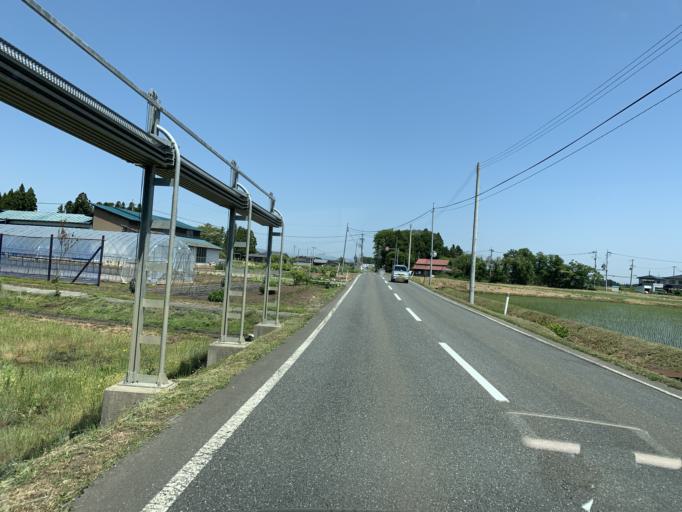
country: JP
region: Iwate
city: Kitakami
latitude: 39.2530
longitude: 141.0653
